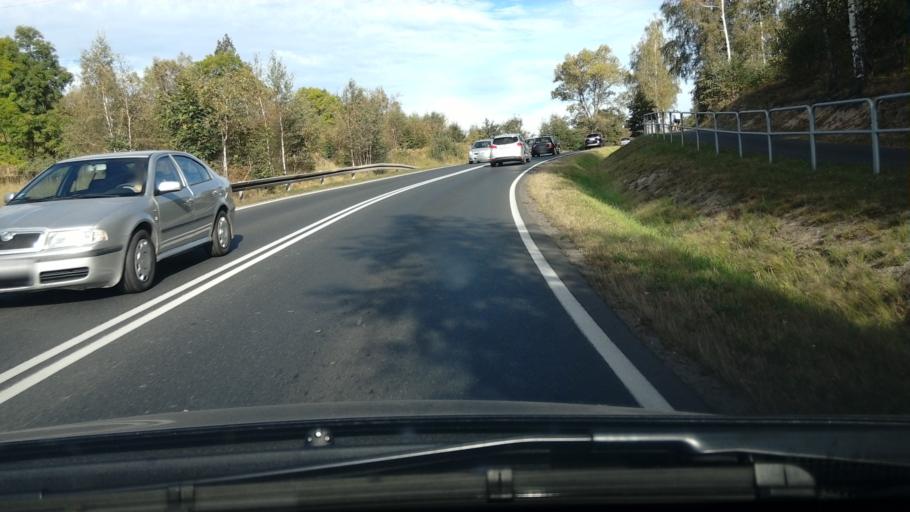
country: PL
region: Lower Silesian Voivodeship
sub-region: Powiat jeleniogorski
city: Myslakowice
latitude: 50.8669
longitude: 15.7678
